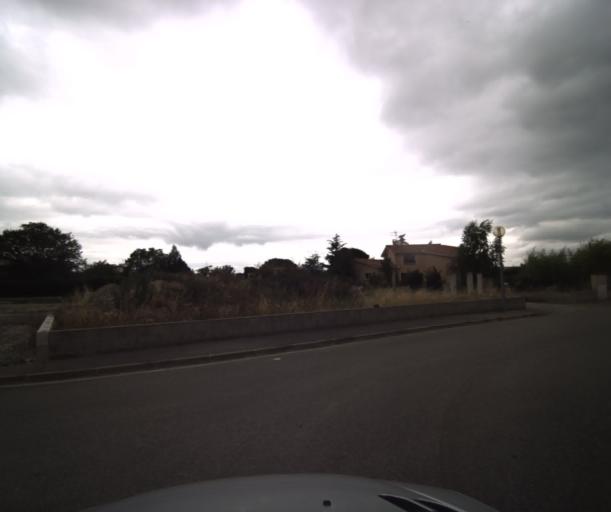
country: FR
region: Midi-Pyrenees
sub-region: Departement de la Haute-Garonne
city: Lacroix-Falgarde
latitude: 43.4947
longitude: 1.3981
